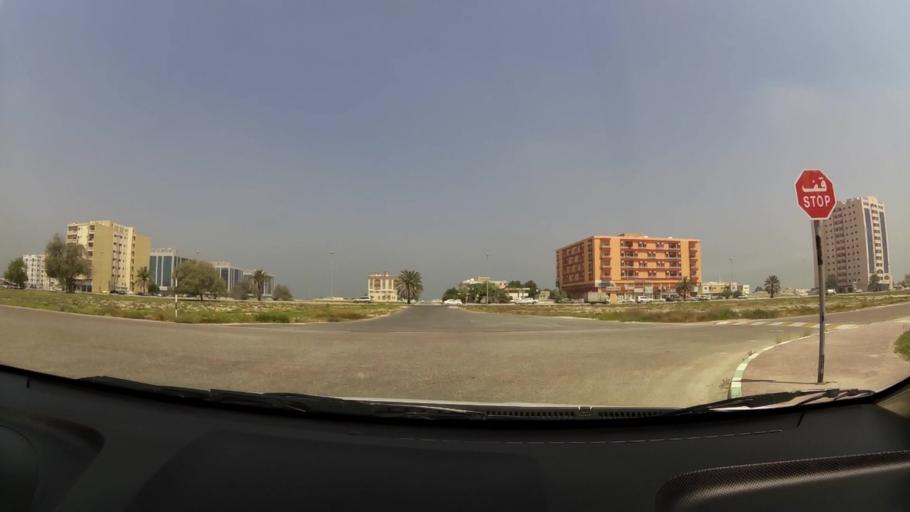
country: AE
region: Umm al Qaywayn
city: Umm al Qaywayn
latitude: 25.5770
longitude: 55.5616
